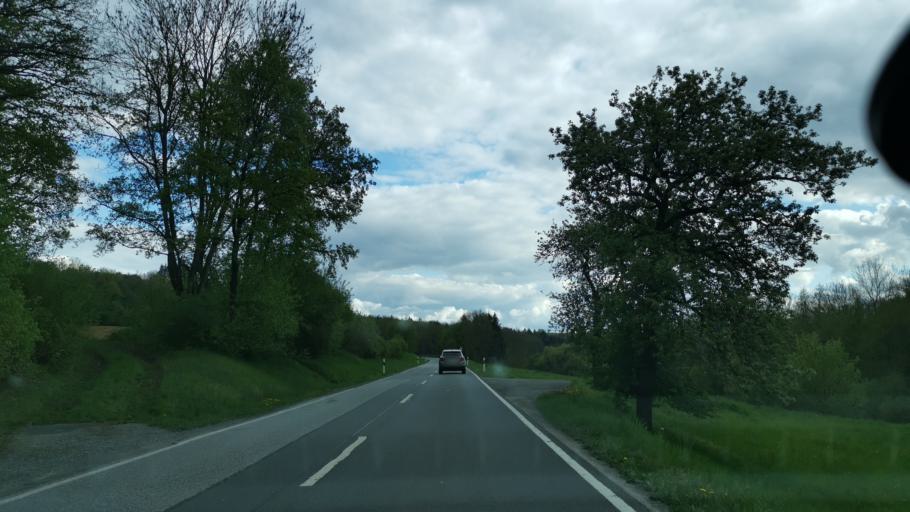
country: DE
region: Baden-Wuerttemberg
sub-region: Karlsruhe Region
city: Osterburken
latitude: 49.4671
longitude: 9.4153
